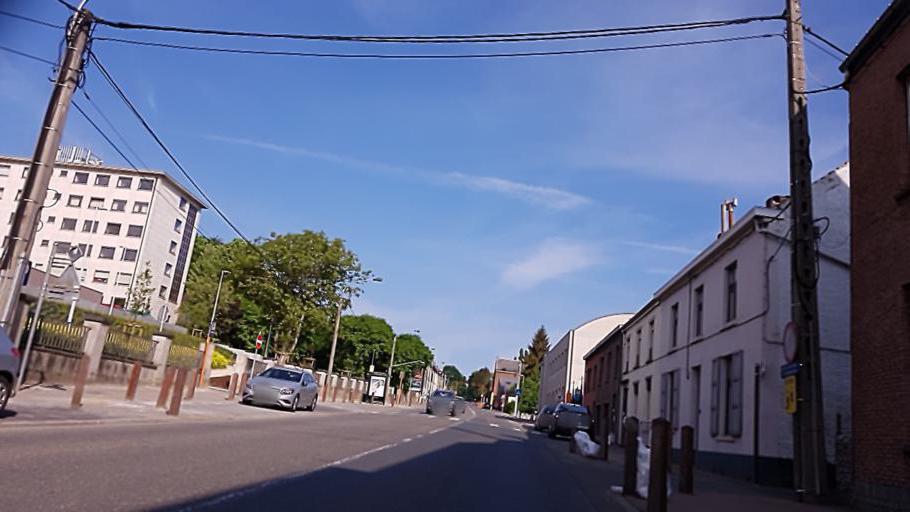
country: BE
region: Wallonia
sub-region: Province du Brabant Wallon
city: Wavre
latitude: 50.7207
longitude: 4.6099
